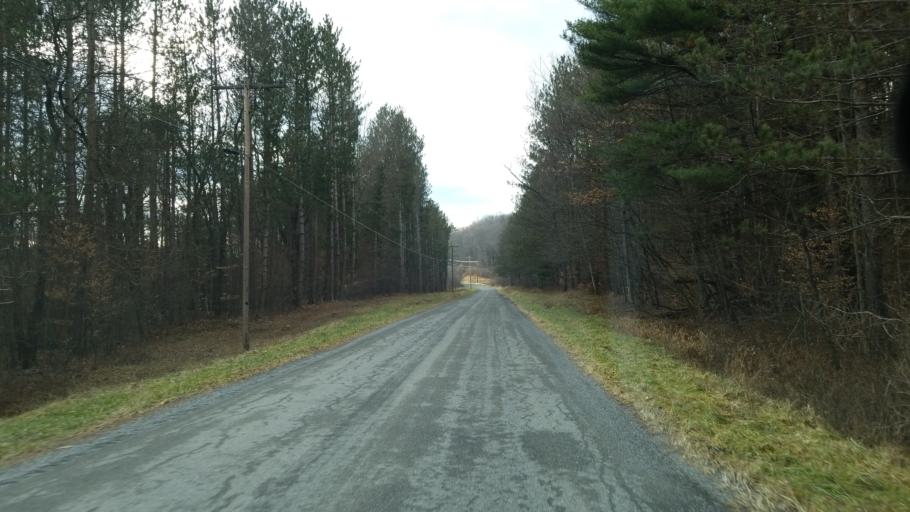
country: US
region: Pennsylvania
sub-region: Clearfield County
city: Treasure Lake
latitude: 41.1277
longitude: -78.6115
